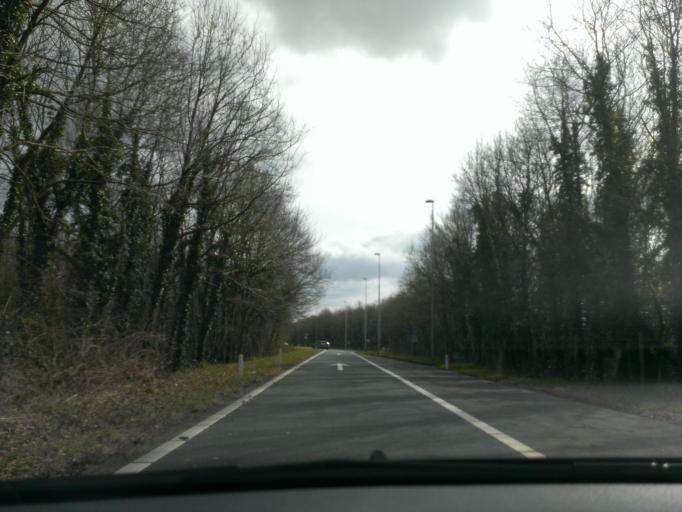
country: NL
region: Overijssel
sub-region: Gemeente Borne
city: Borne
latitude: 52.2929
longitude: 6.7276
